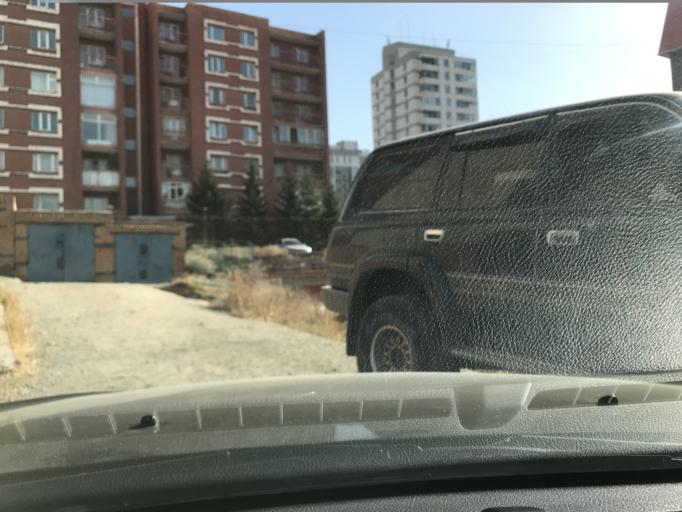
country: MN
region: Ulaanbaatar
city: Ulaanbaatar
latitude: 47.9215
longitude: 106.9450
